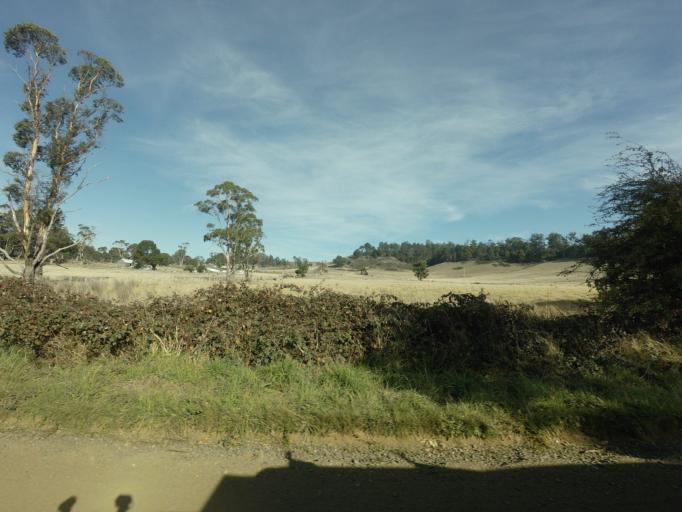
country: AU
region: Tasmania
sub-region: Sorell
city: Sorell
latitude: -42.4789
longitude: 147.4789
